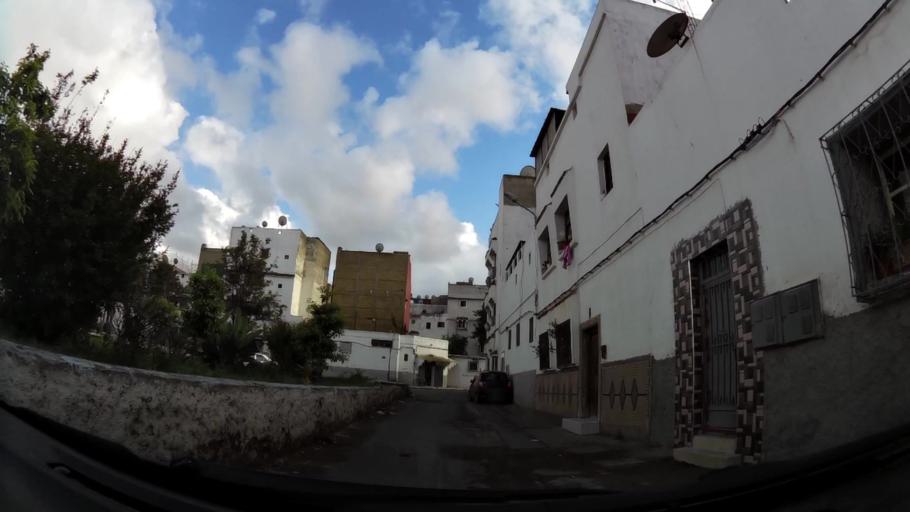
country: MA
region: Grand Casablanca
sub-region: Casablanca
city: Casablanca
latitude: 33.5540
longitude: -7.5949
